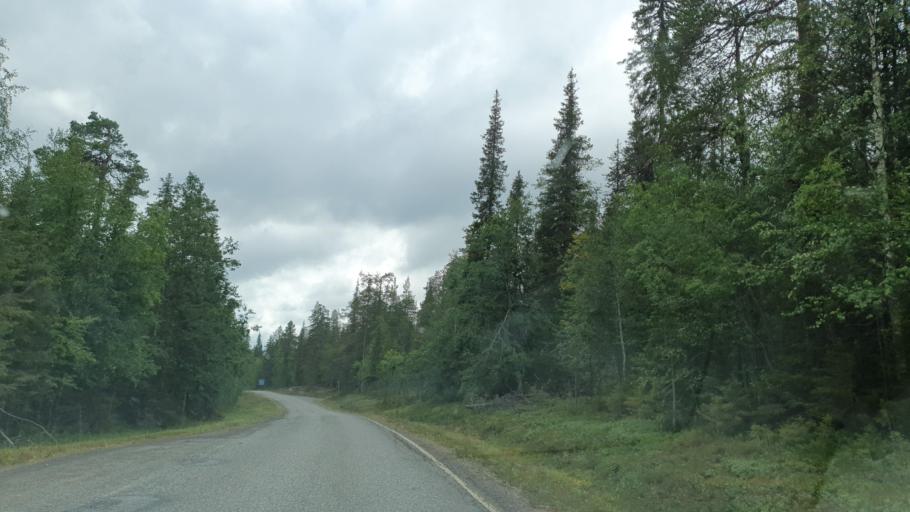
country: FI
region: Lapland
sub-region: Tunturi-Lappi
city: Muonio
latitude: 67.7264
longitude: 24.2395
